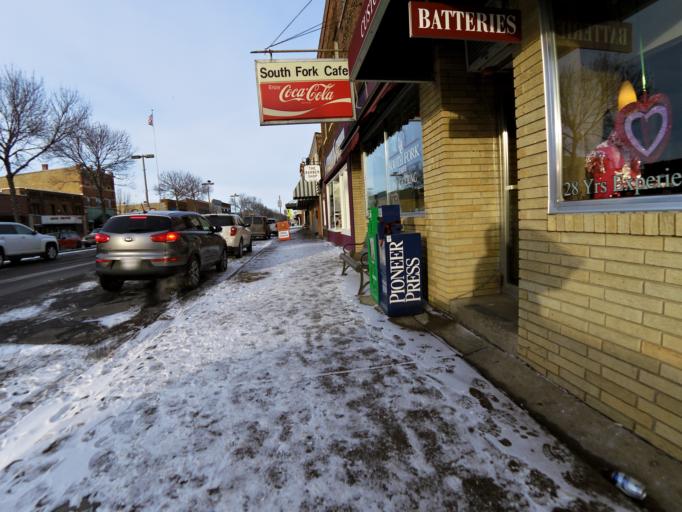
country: US
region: Wisconsin
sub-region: Pierce County
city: River Falls
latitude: 44.8579
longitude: -92.6262
